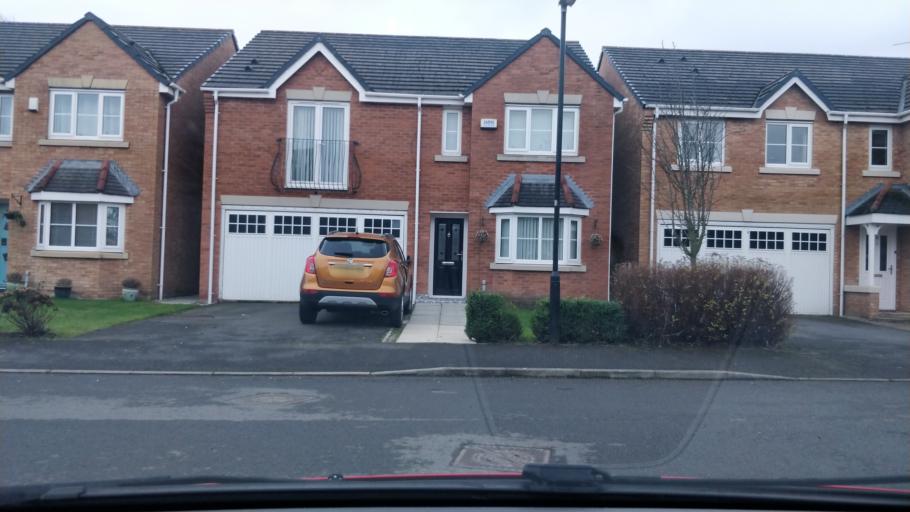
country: GB
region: England
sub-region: Sefton
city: Southport
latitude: 53.6237
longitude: -2.9993
